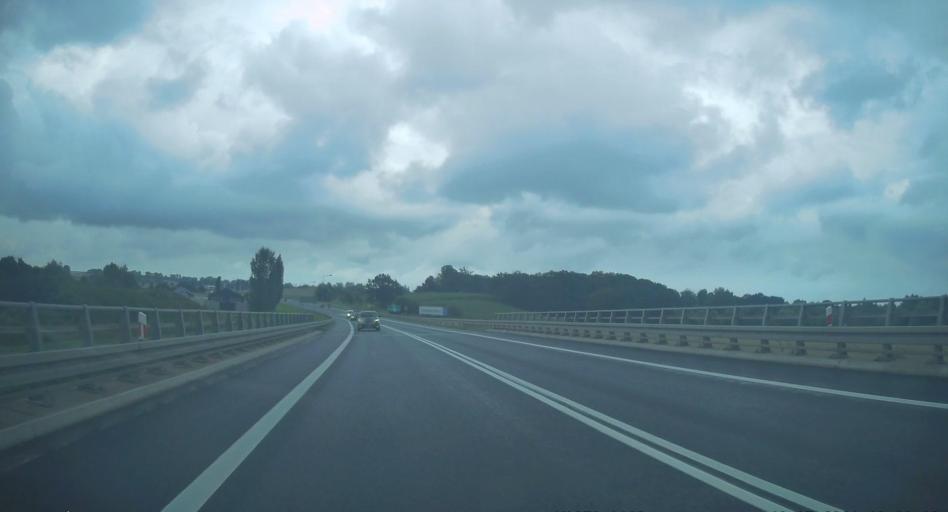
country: PL
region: Opole Voivodeship
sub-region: Powiat nyski
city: Otmuchow
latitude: 50.4585
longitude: 17.1925
